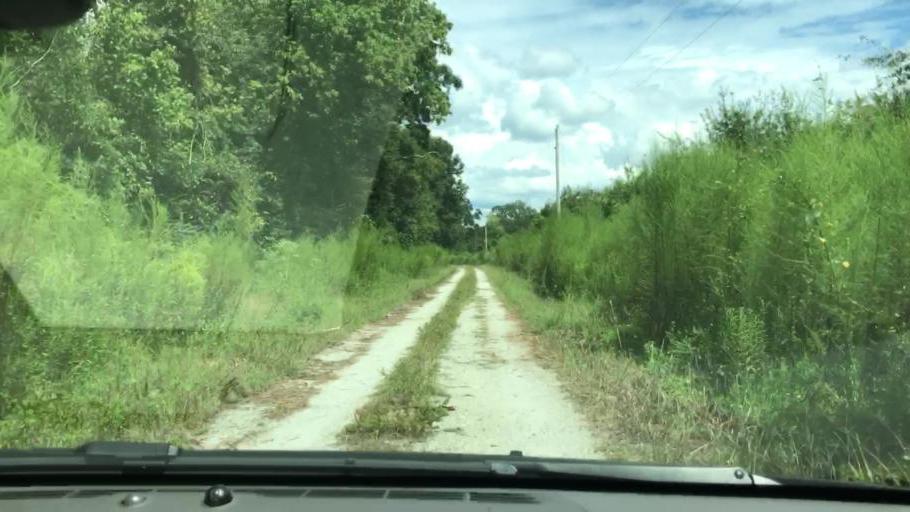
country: US
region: Georgia
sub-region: Quitman County
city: Georgetown
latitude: 31.9950
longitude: -85.0477
